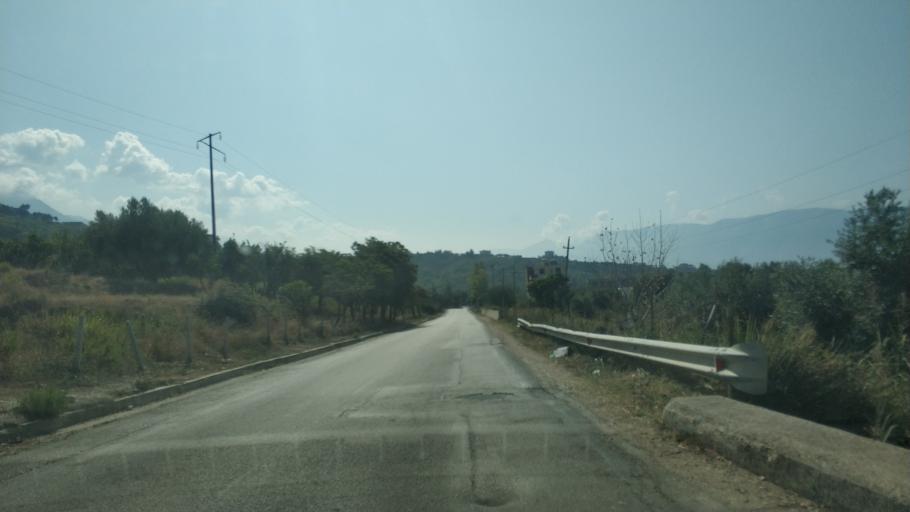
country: AL
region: Vlore
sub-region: Rrethi i Vlores
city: Orikum
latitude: 40.3760
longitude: 19.4819
